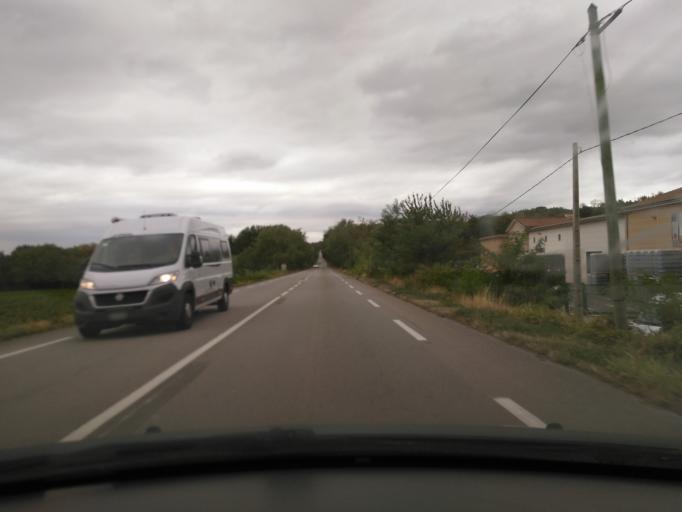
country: FR
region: Rhone-Alpes
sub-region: Departement de la Drome
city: La Garde-Adhemar
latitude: 44.4194
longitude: 4.7888
